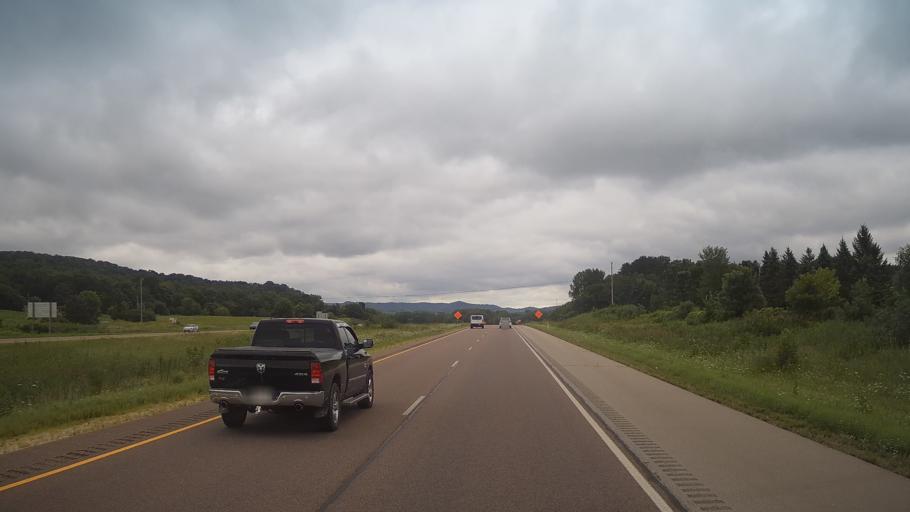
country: US
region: Wisconsin
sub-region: La Crosse County
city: Onalaska
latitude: 43.8736
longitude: -91.1614
